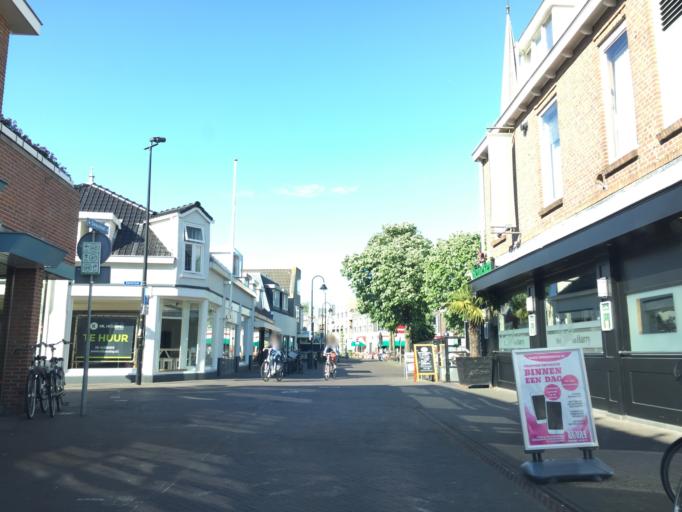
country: NL
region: South Holland
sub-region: Gemeente Noordwijkerhout
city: Noordwijkerhout
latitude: 52.2623
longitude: 4.4923
